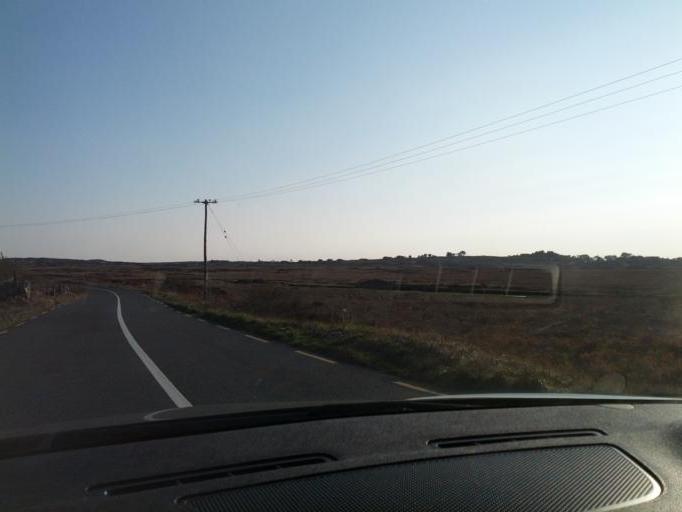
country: IE
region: Connaught
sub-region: County Galway
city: Oughterard
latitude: 53.3103
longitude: -9.5544
